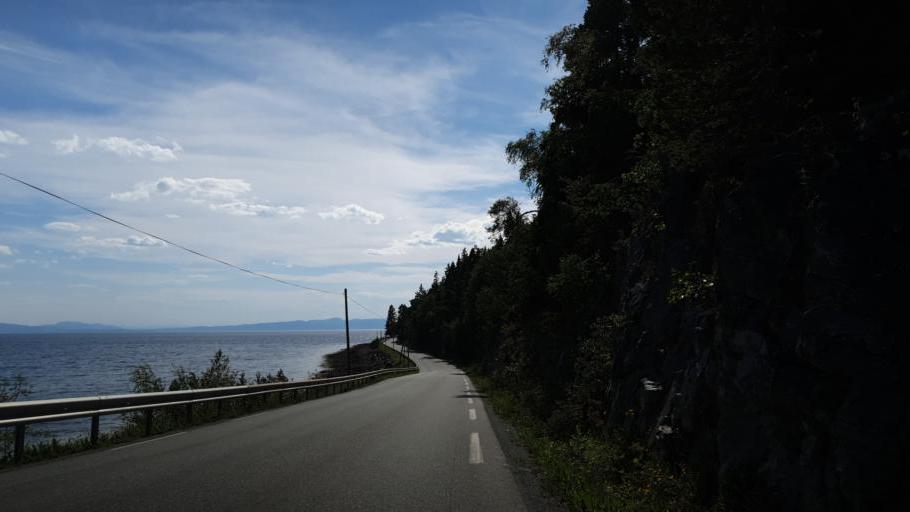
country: NO
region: Nord-Trondelag
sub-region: Leksvik
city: Leksvik
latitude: 63.6431
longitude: 10.5935
